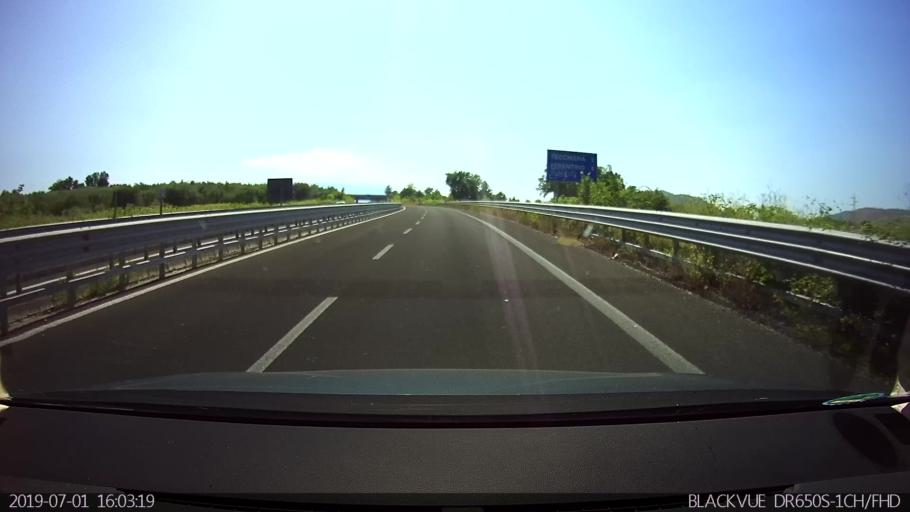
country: IT
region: Latium
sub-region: Provincia di Frosinone
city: Tecchiena
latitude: 41.6733
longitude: 13.3357
